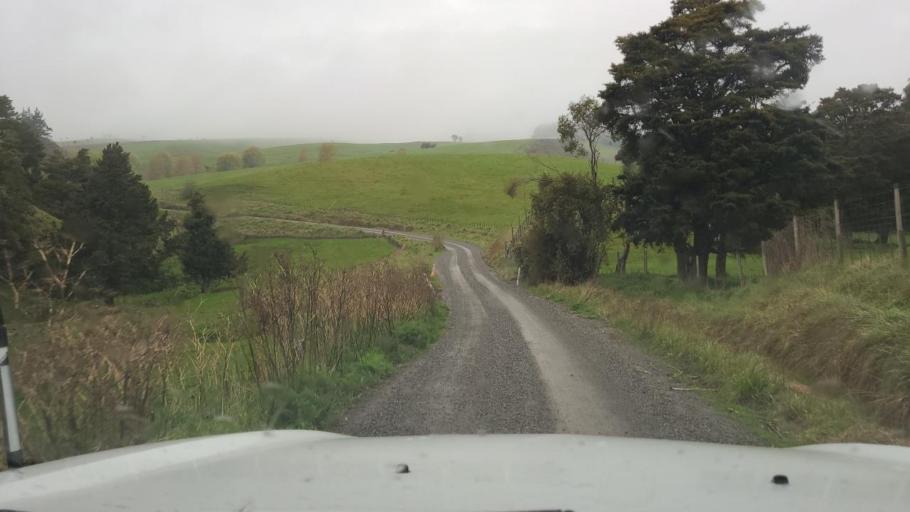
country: NZ
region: Wellington
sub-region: Masterton District
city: Masterton
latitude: -41.0865
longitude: 175.7209
